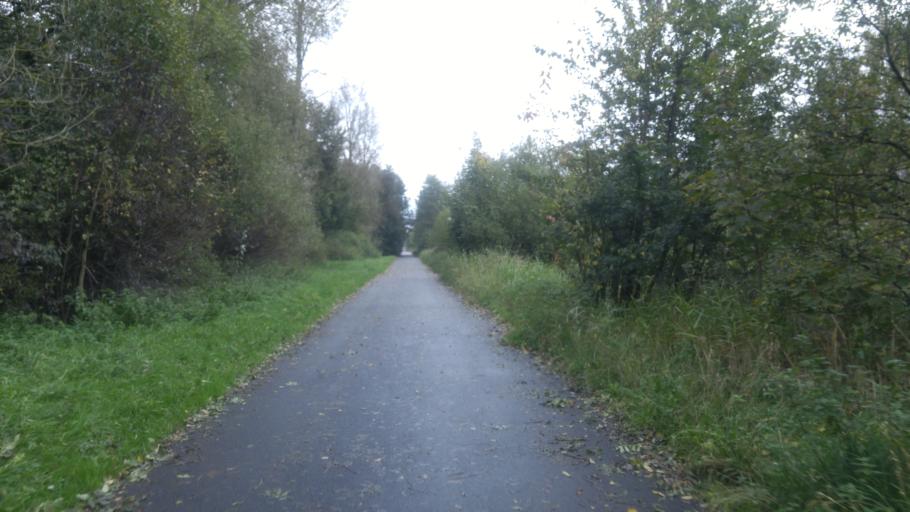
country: DE
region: Bremen
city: Bremen
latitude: 53.1086
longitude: 8.8437
